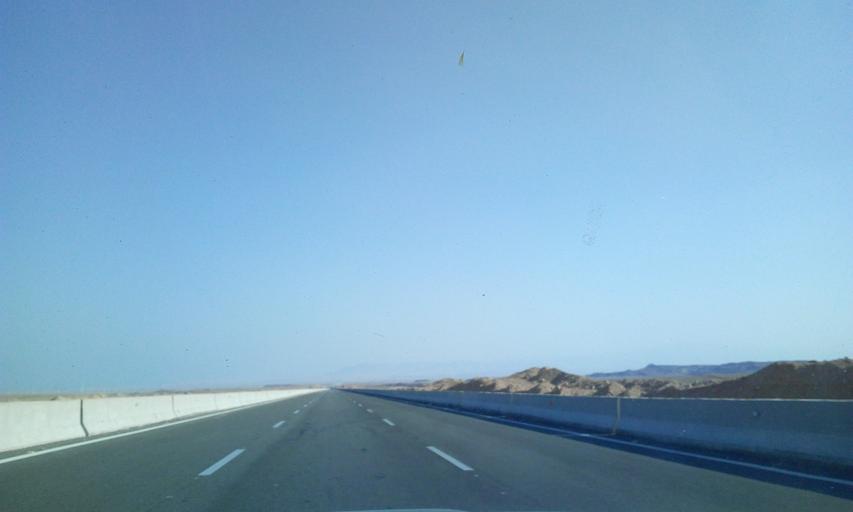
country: EG
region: As Suways
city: Ain Sukhna
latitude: 29.2475
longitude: 32.4796
